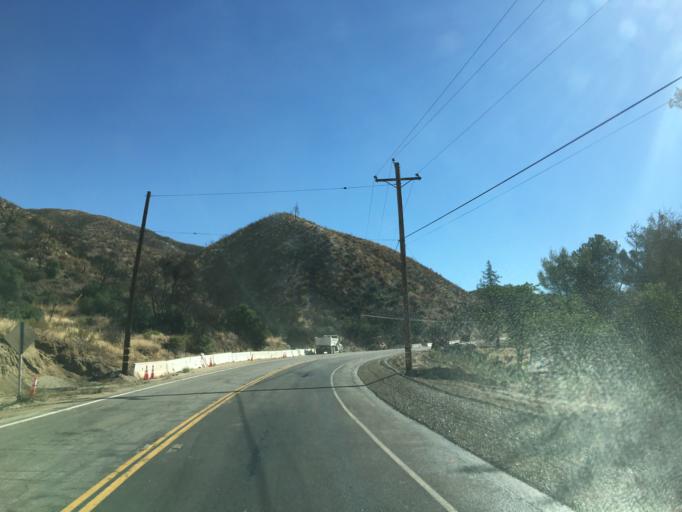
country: US
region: California
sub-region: Los Angeles County
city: Green Valley
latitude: 34.6533
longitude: -118.4803
